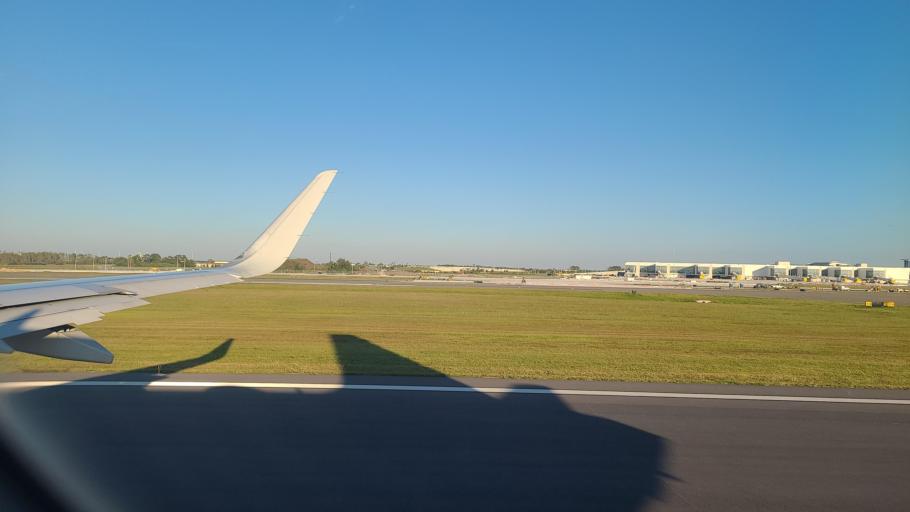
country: US
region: Florida
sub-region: Orange County
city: Taft
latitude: 28.4178
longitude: -81.3220
